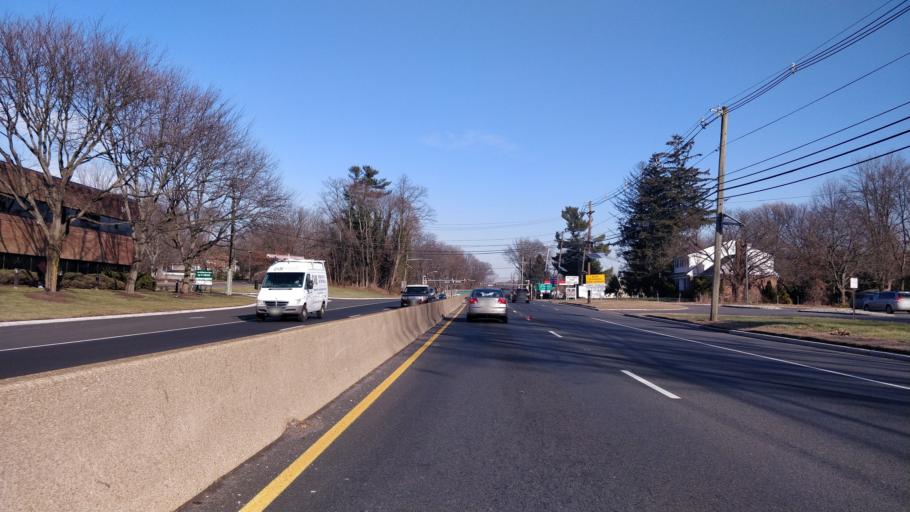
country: US
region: New Jersey
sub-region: Union County
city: Mountainside
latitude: 40.6706
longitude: -74.3599
